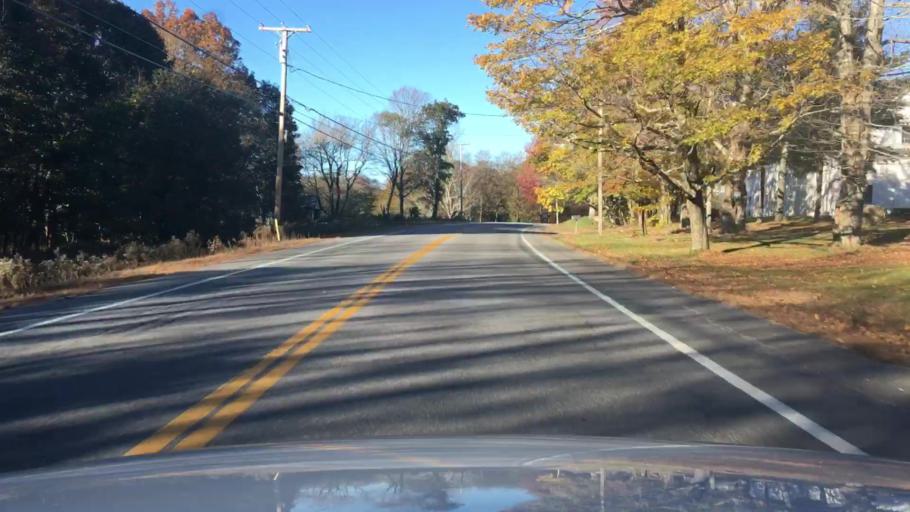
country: US
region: Maine
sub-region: Sagadahoc County
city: Topsham
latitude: 44.0481
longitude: -69.9401
